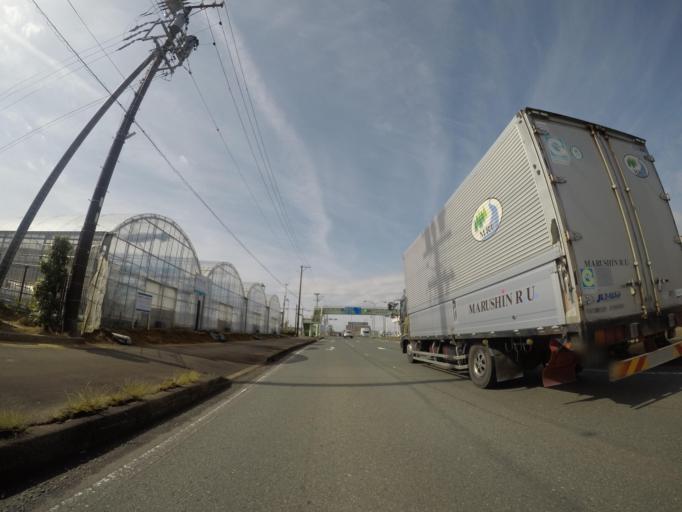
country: JP
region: Shizuoka
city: Hamamatsu
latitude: 34.7707
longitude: 137.6910
